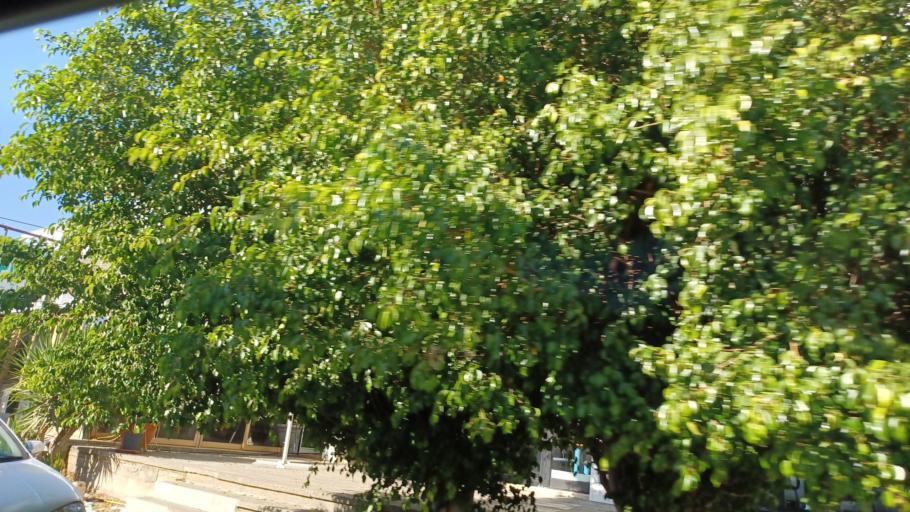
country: CY
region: Limassol
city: Limassol
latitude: 34.6751
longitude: 33.0097
